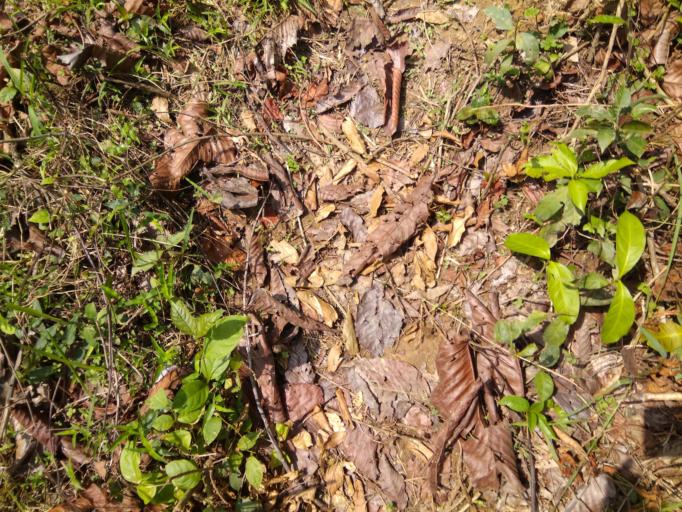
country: BD
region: Chittagong
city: Cox's Bazar
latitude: 21.7109
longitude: 92.0847
